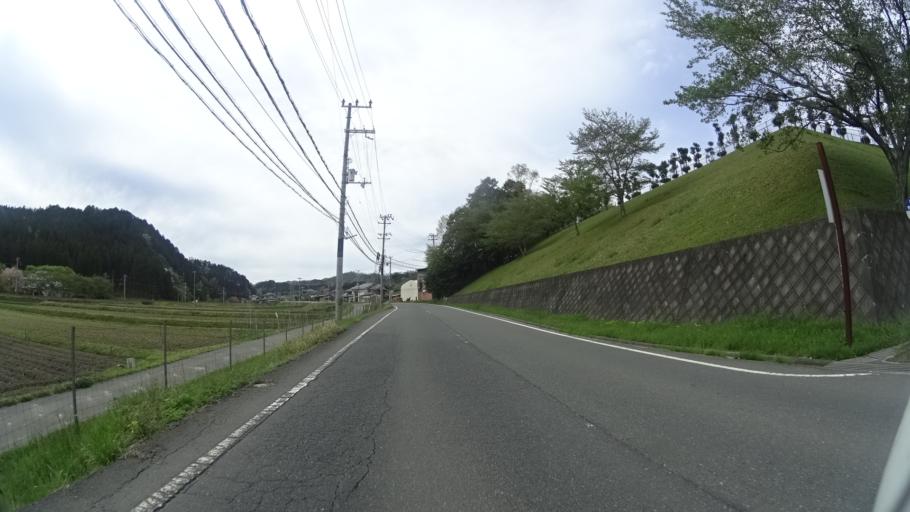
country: JP
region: Kyoto
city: Kameoka
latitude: 35.1894
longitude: 135.4828
